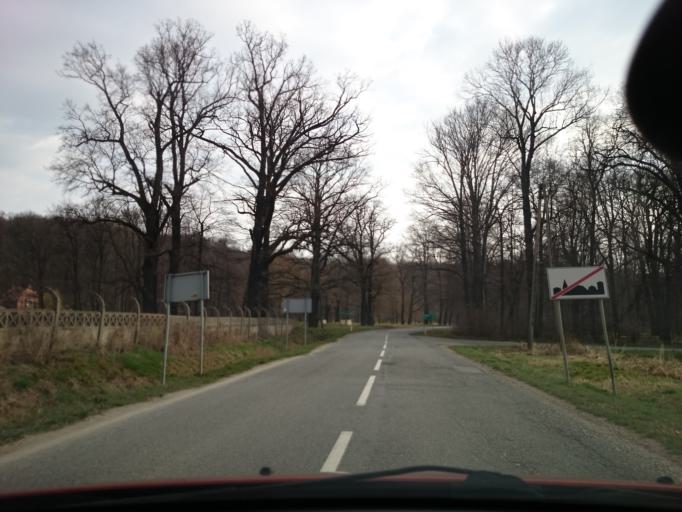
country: PL
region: Lower Silesian Voivodeship
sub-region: Powiat zabkowicki
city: Kamieniec Zabkowicki
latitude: 50.5177
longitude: 16.8808
